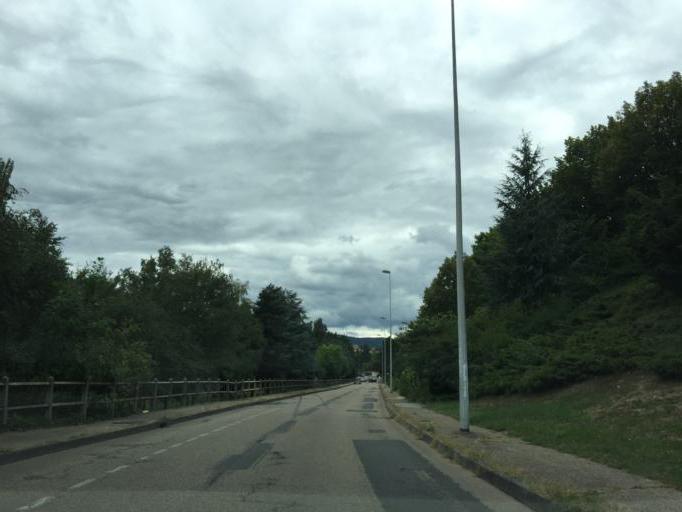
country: FR
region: Rhone-Alpes
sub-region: Departement de la Loire
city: Saint-Chamond
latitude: 45.4750
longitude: 4.5359
